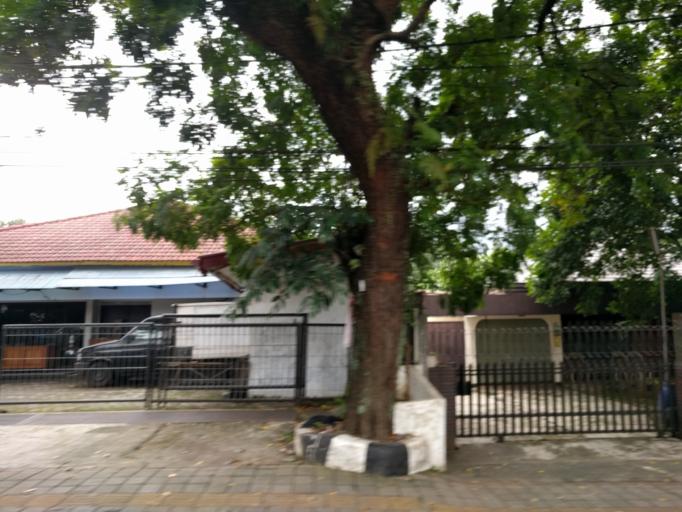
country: ID
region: West Java
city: Bogor
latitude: -6.5913
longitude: 106.8071
